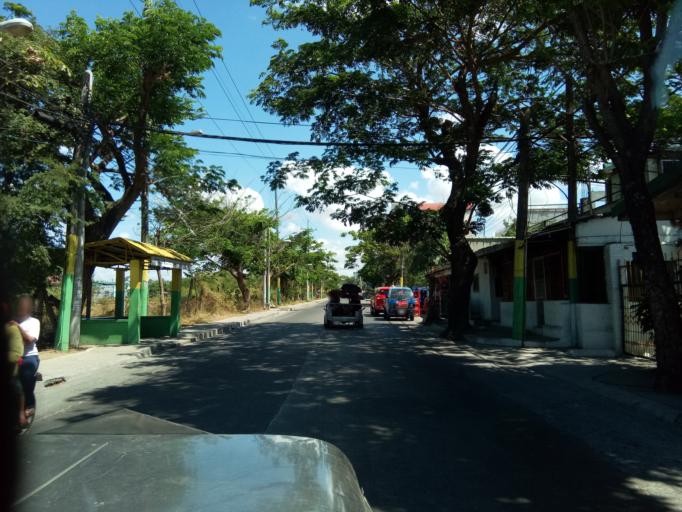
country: PH
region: Calabarzon
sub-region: Province of Cavite
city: Dasmarinas
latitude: 14.3463
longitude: 120.9460
